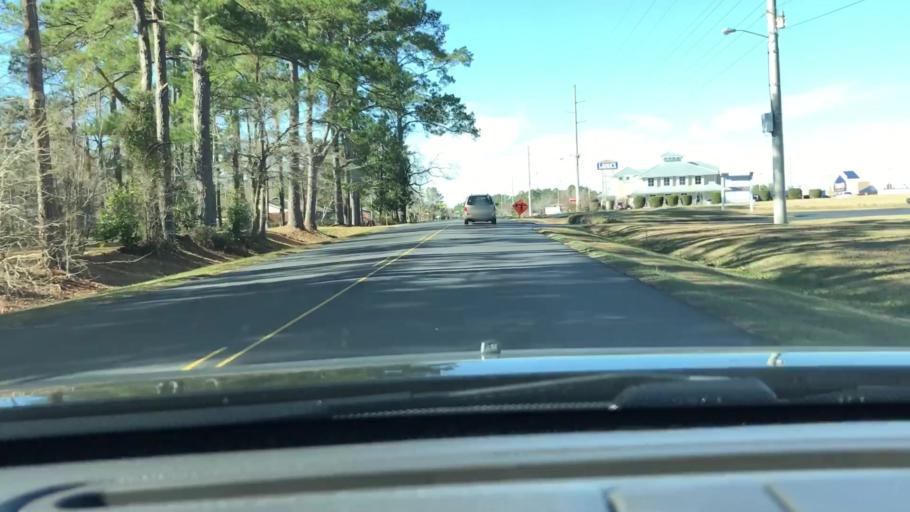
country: US
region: North Carolina
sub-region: Brunswick County
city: Shallotte
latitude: 33.9717
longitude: -78.3974
